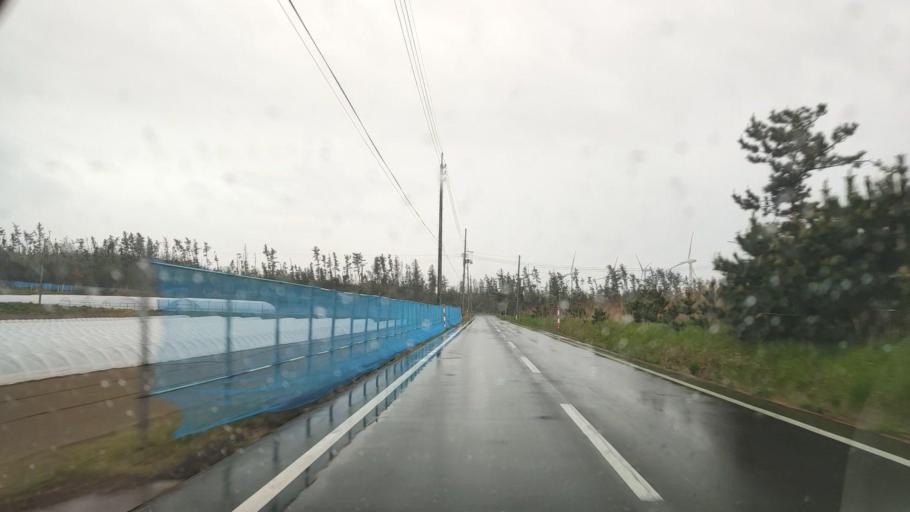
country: JP
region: Akita
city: Noshiromachi
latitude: 40.0823
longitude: 139.9558
